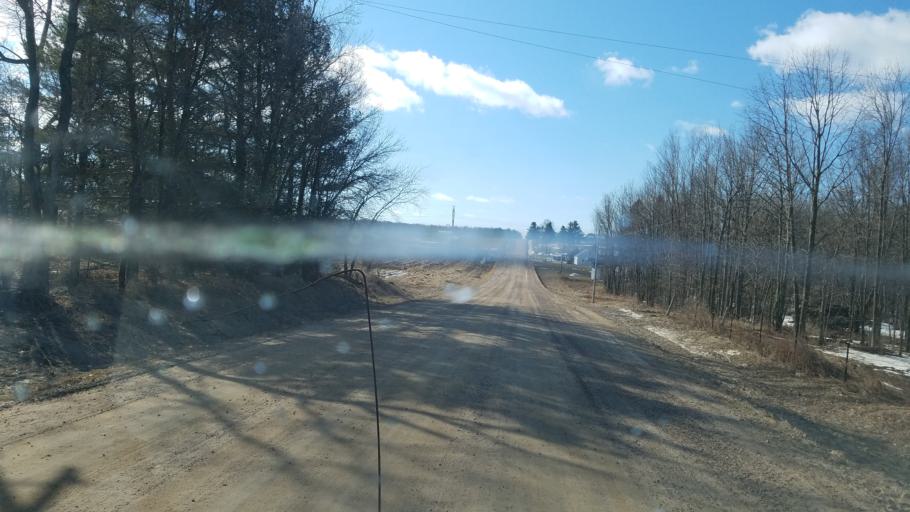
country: US
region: Wisconsin
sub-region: Clark County
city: Loyal
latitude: 44.6733
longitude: -90.4559
